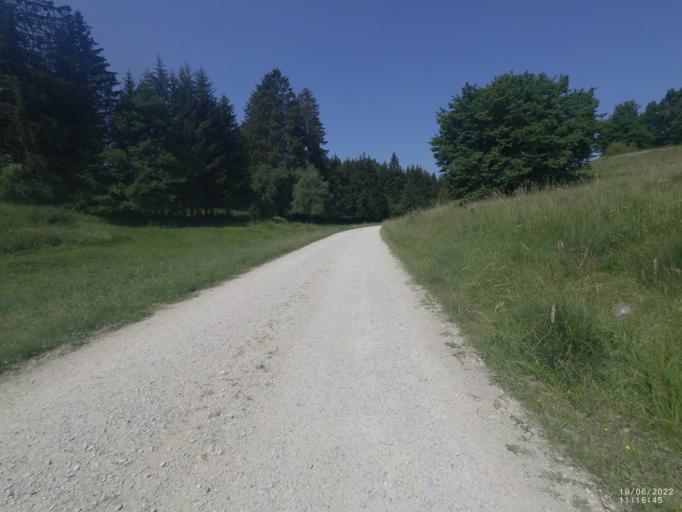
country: DE
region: Baden-Wuerttemberg
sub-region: Regierungsbezirk Stuttgart
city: Gerstetten
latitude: 48.6081
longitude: 9.9863
